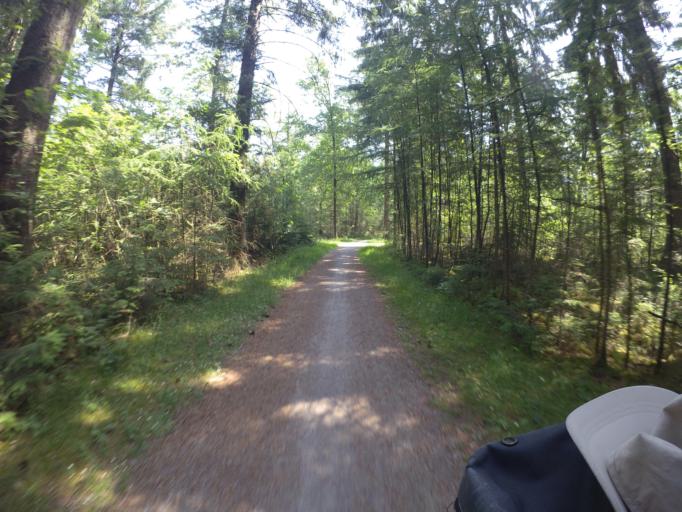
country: NL
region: Drenthe
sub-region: Gemeente De Wolden
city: Ruinen
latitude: 52.7292
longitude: 6.3732
